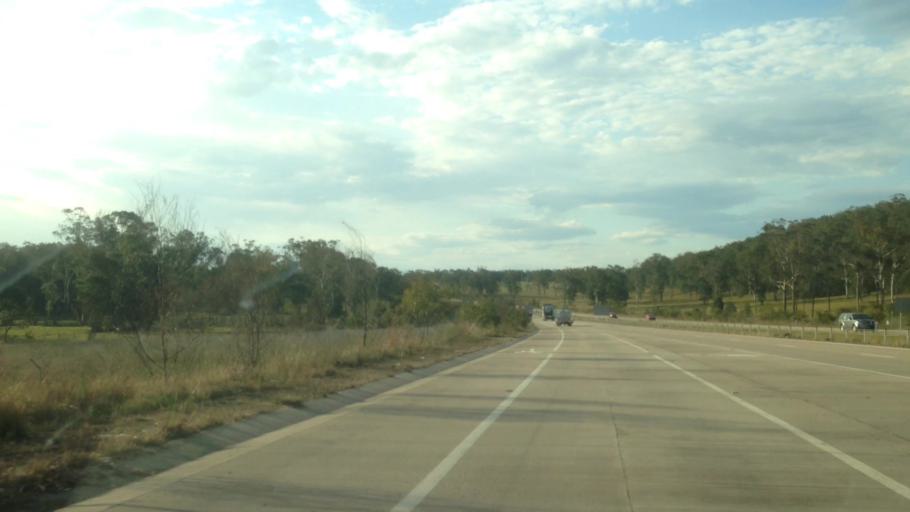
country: AU
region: New South Wales
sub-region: Cessnock
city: Heddon Greta
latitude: -32.8418
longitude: 151.5419
